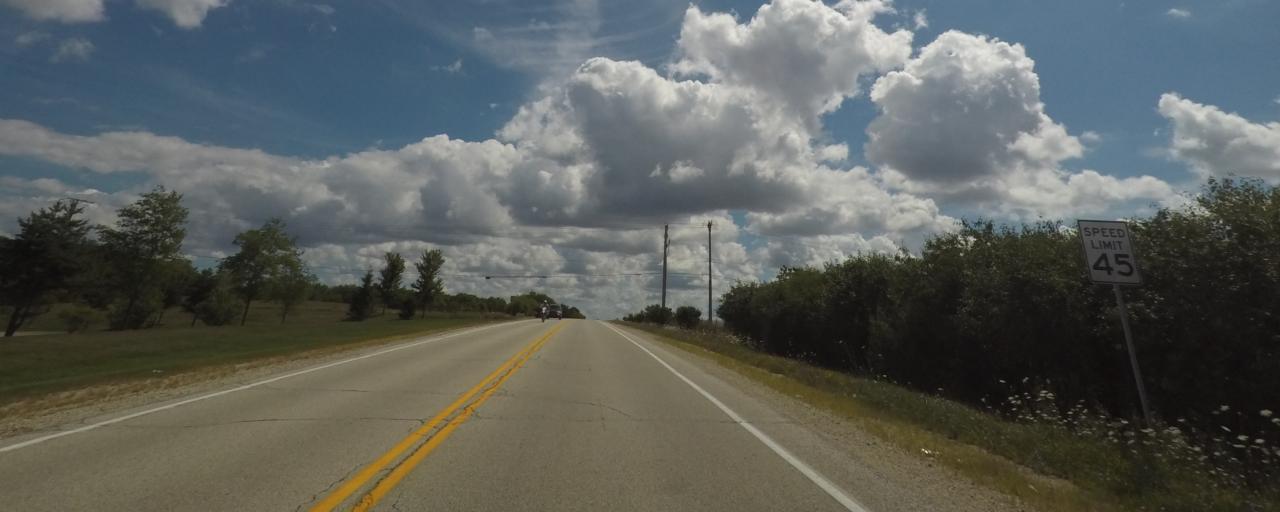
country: US
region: Wisconsin
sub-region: Waukesha County
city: Pewaukee
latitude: 43.0464
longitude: -88.2671
